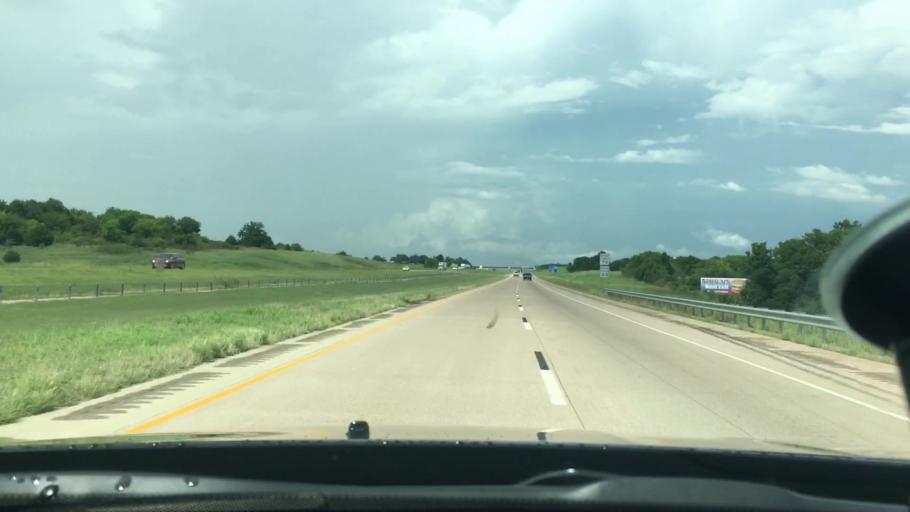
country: US
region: Oklahoma
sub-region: Garvin County
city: Pauls Valley
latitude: 34.7148
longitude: -97.2500
